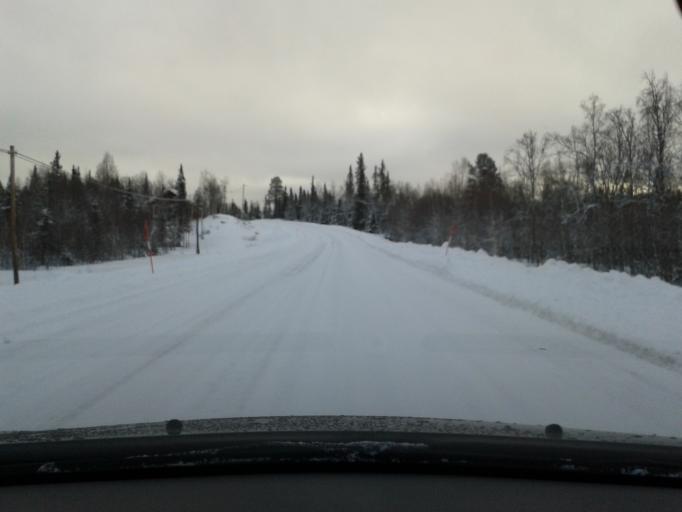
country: SE
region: Vaesterbotten
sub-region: Vilhelmina Kommun
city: Sjoberg
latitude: 65.2496
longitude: 15.7343
